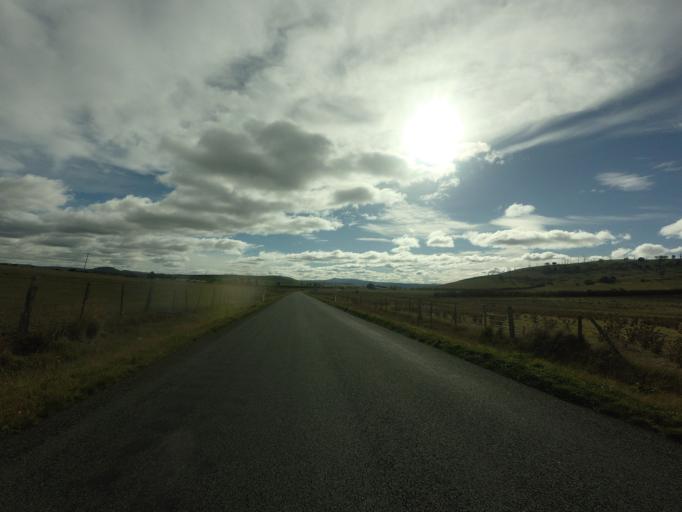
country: AU
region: Tasmania
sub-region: Brighton
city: Bridgewater
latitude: -42.3688
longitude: 147.3493
